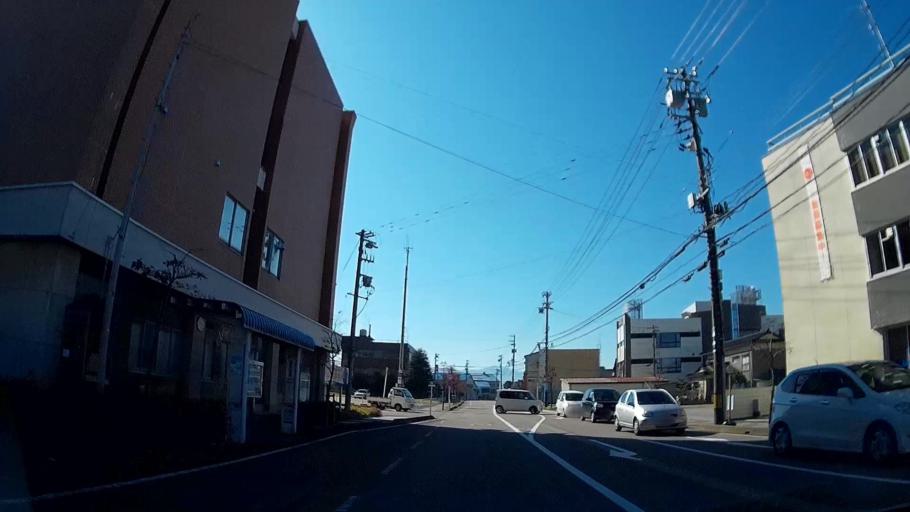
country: JP
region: Toyama
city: Nanto-shi
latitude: 36.5881
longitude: 136.9189
